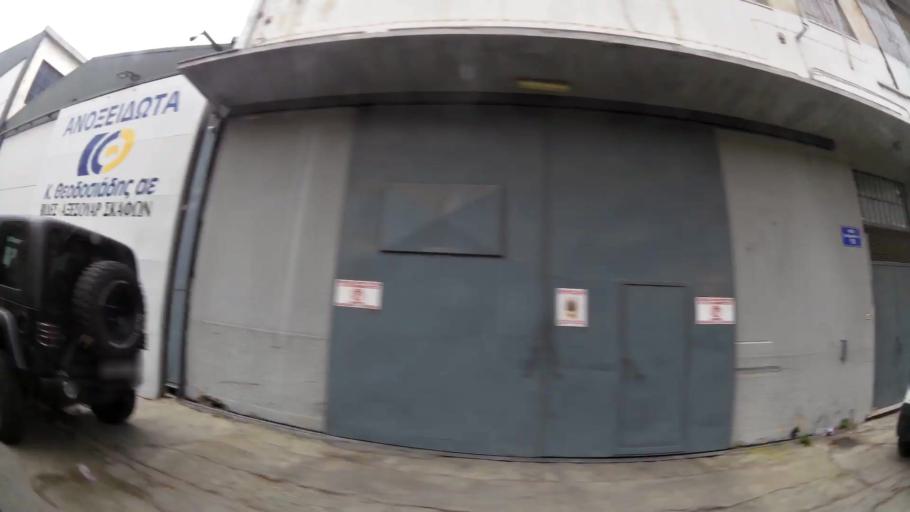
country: GR
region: Attica
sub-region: Nomos Attikis
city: Piraeus
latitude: 37.9525
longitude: 23.6448
